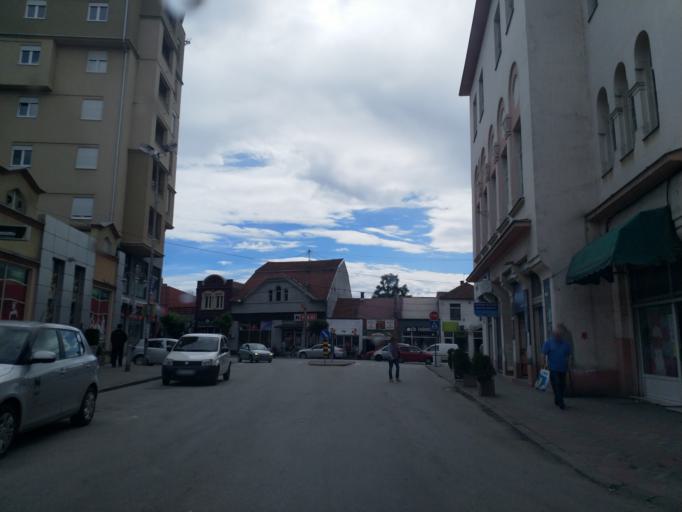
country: RS
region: Central Serbia
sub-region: Pomoravski Okrug
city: Jagodina
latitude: 43.9804
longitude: 21.2594
